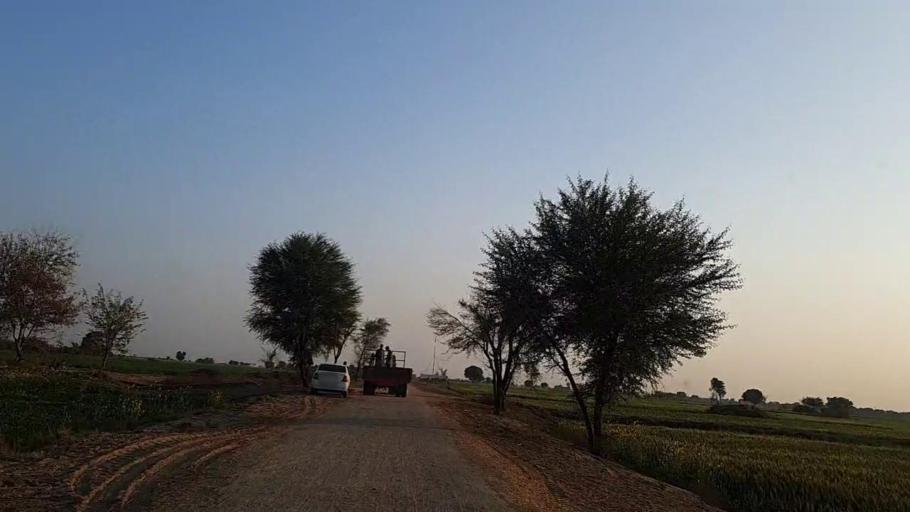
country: PK
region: Sindh
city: Shahdadpur
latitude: 26.0064
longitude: 68.4918
